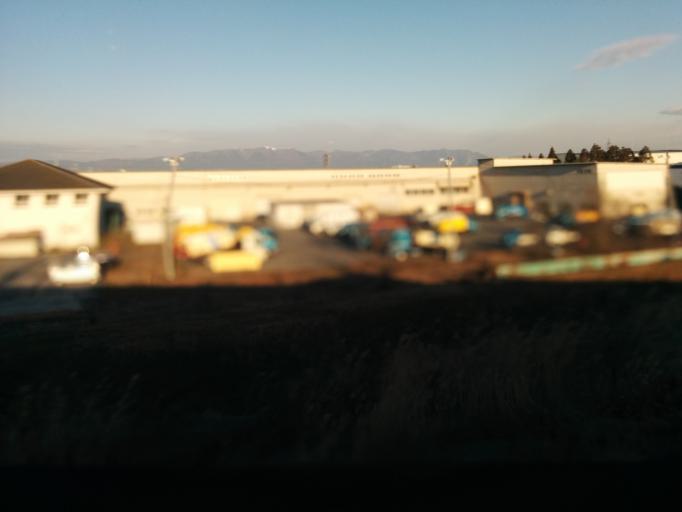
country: JP
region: Shiga Prefecture
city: Omihachiman
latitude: 35.0811
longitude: 136.0495
